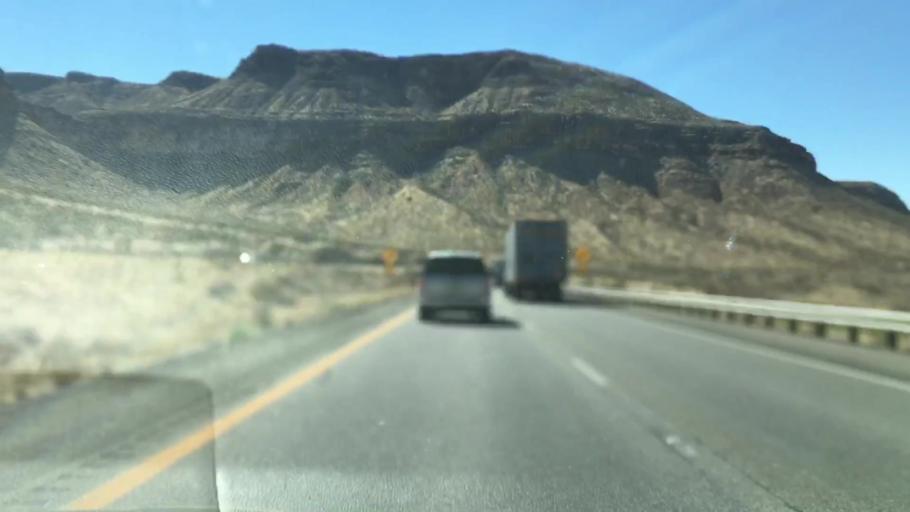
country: US
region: Utah
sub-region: Washington County
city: Santa Clara
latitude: 36.9743
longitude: -113.6863
